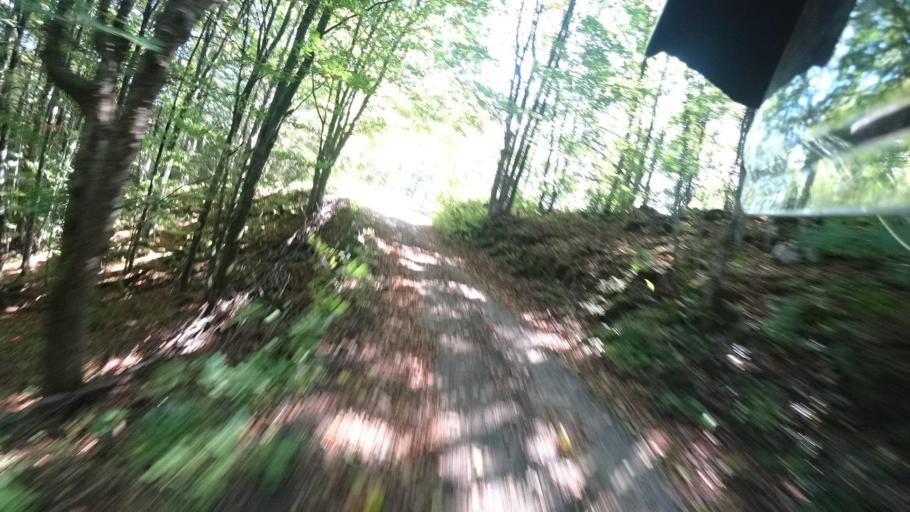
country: HR
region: Karlovacka
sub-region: Grad Ogulin
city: Ogulin
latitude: 45.1965
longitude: 15.1083
